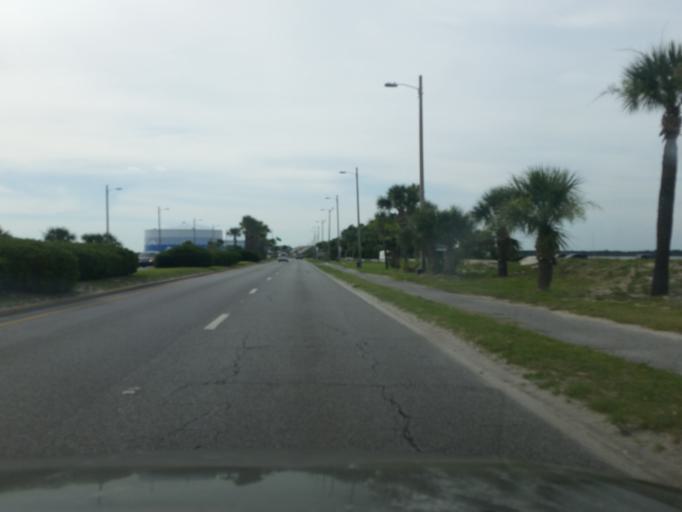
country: US
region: Florida
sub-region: Santa Rosa County
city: Gulf Breeze
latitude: 30.3378
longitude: -87.1454
